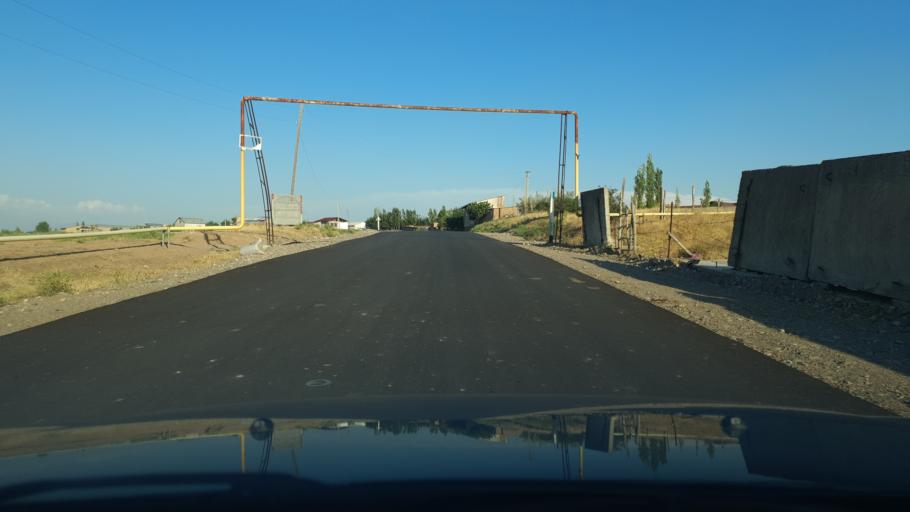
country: UZ
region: Toshkent
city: Salor
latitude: 41.4581
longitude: 69.3949
